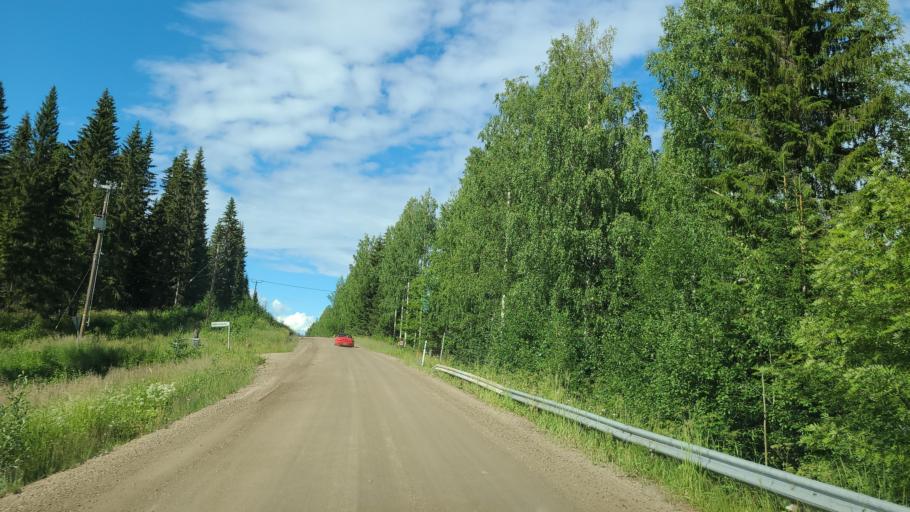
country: FI
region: Northern Savo
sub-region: Koillis-Savo
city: Kaavi
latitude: 62.9357
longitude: 28.7630
